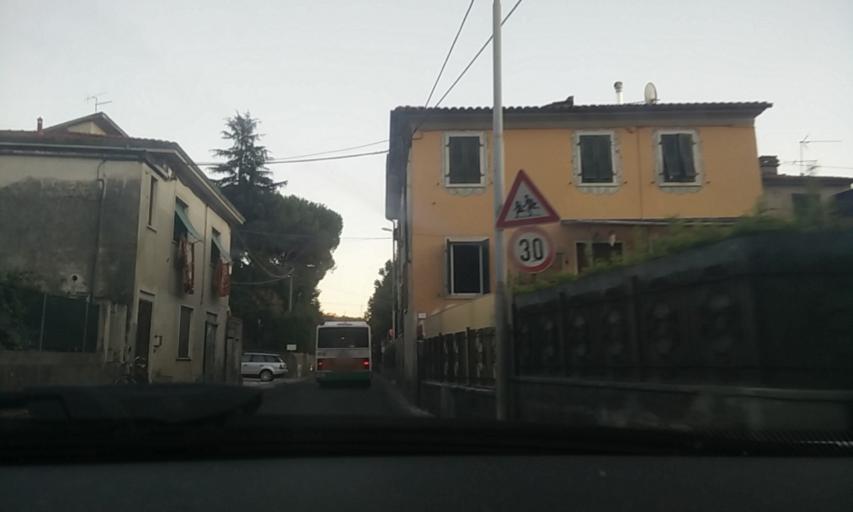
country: IT
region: Tuscany
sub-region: Provincia di Massa-Carrara
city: Carrara
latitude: 44.0645
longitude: 10.0839
